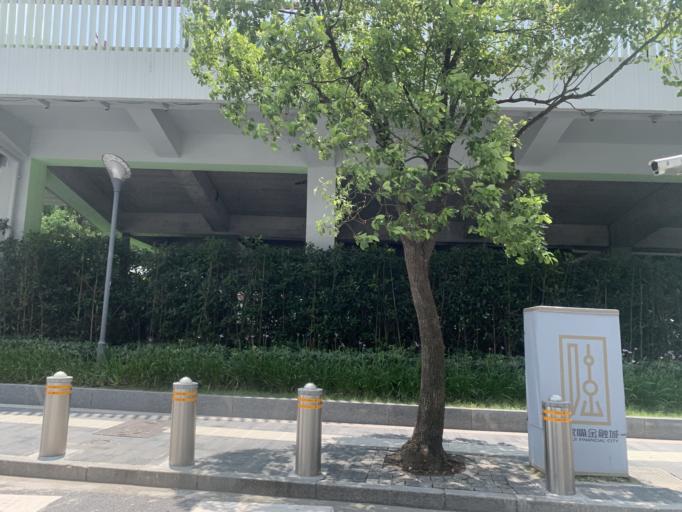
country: CN
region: Shanghai Shi
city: Hongkou
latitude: 31.2333
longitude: 121.4983
